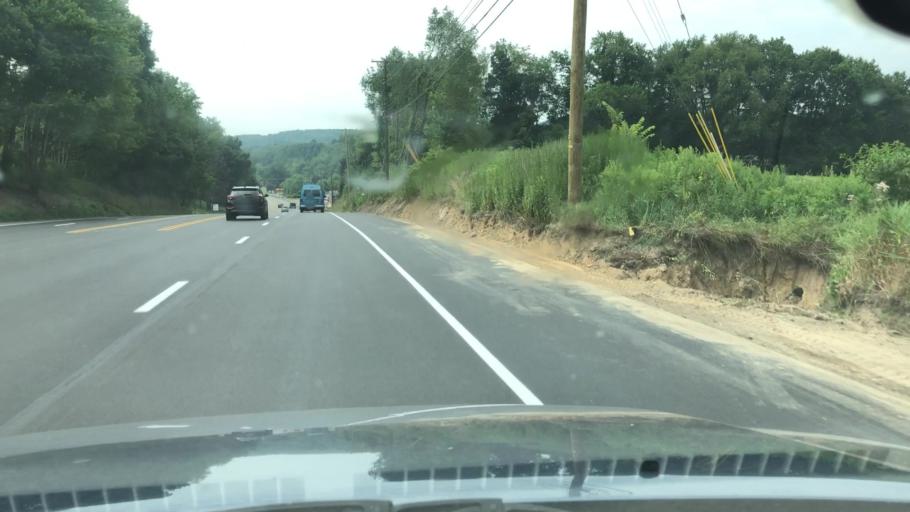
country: US
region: Pennsylvania
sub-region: Allegheny County
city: Bakerstown
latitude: 40.6938
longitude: -79.9378
